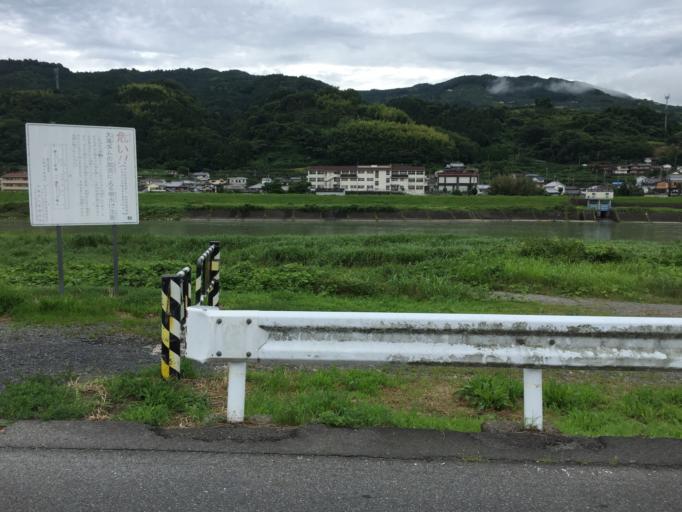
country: JP
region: Wakayama
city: Hashimoto
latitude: 34.3115
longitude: 135.6054
